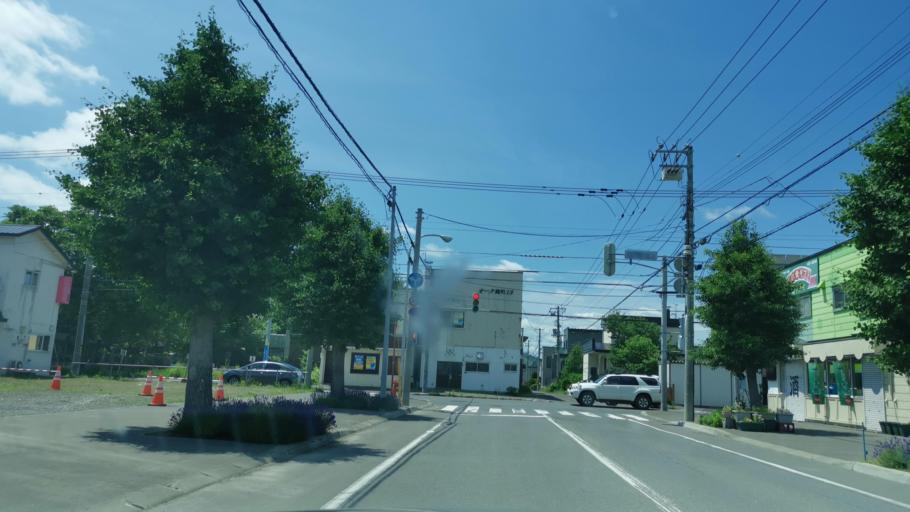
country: JP
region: Hokkaido
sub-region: Asahikawa-shi
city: Asahikawa
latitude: 43.7886
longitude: 142.3414
